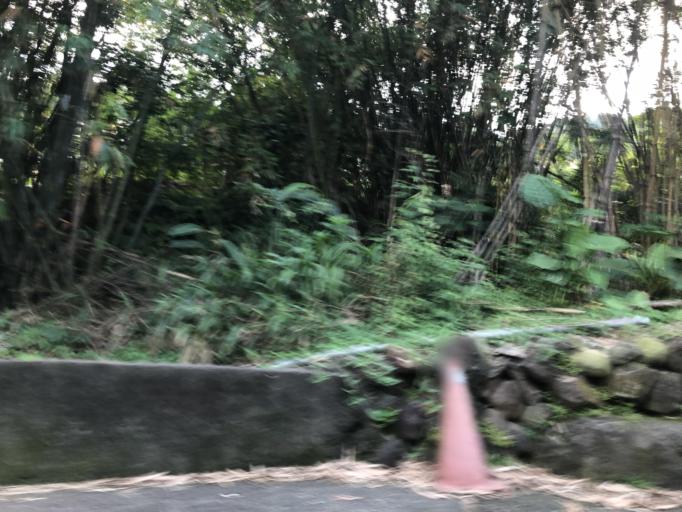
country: TW
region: Taiwan
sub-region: Keelung
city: Keelung
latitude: 25.1920
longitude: 121.6432
